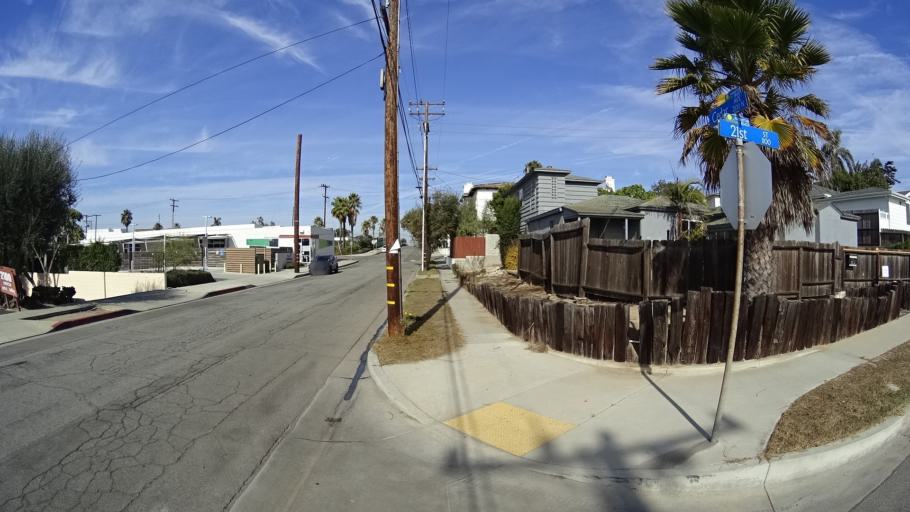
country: US
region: California
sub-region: Los Angeles County
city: Manhattan Beach
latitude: 33.8929
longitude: -118.3947
